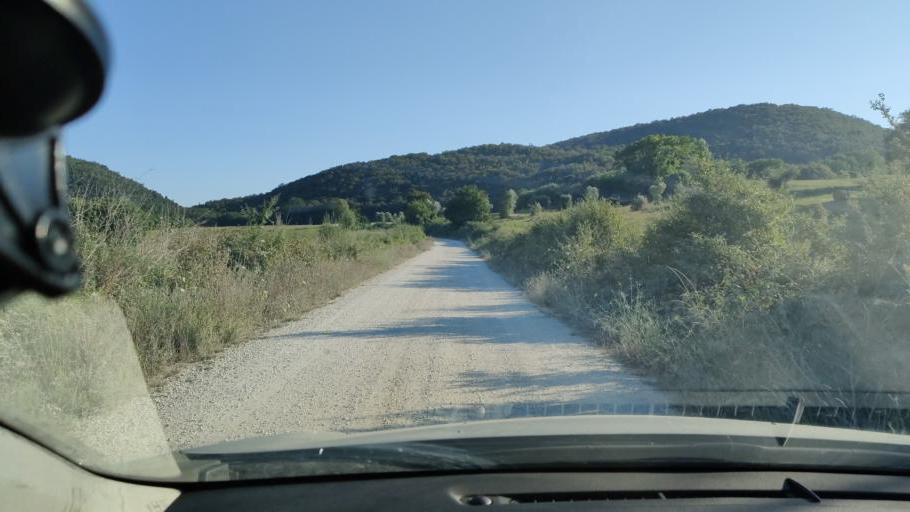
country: IT
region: Umbria
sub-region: Provincia di Terni
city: Amelia
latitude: 42.5438
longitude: 12.3871
